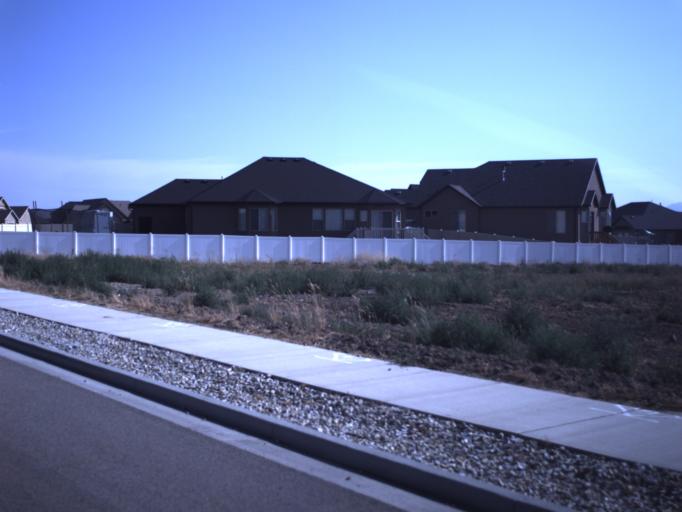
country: US
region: Utah
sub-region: Salt Lake County
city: Herriman
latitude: 40.5147
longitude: -112.0046
